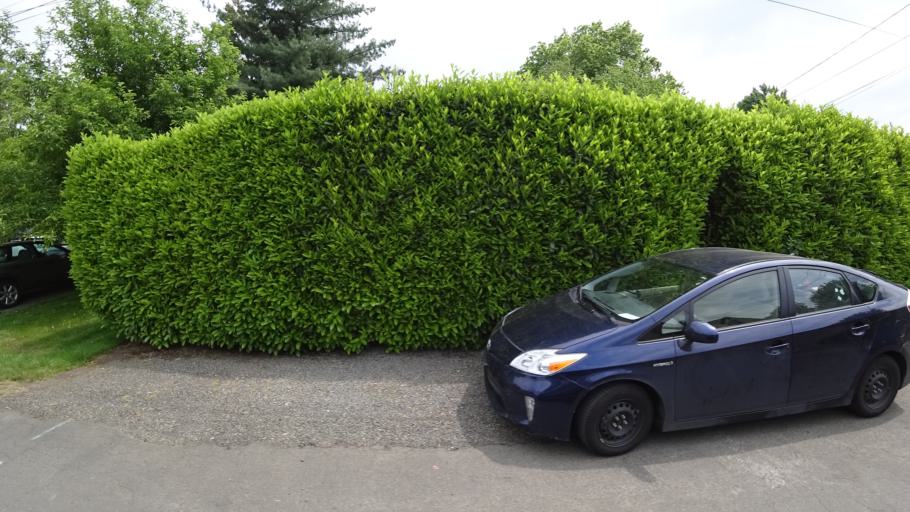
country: US
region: Oregon
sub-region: Washington County
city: Garden Home-Whitford
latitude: 45.4758
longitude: -122.7325
